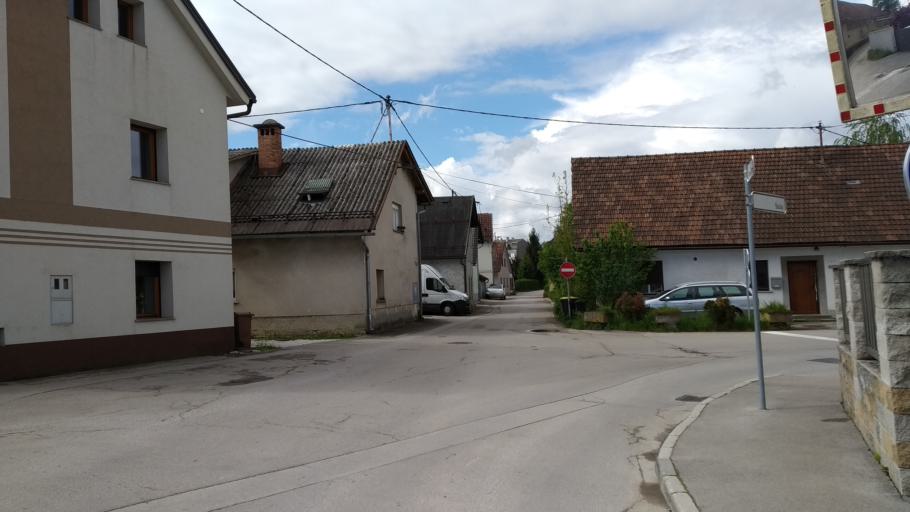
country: SI
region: Ljubljana
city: Ljubljana
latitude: 46.0958
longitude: 14.4733
